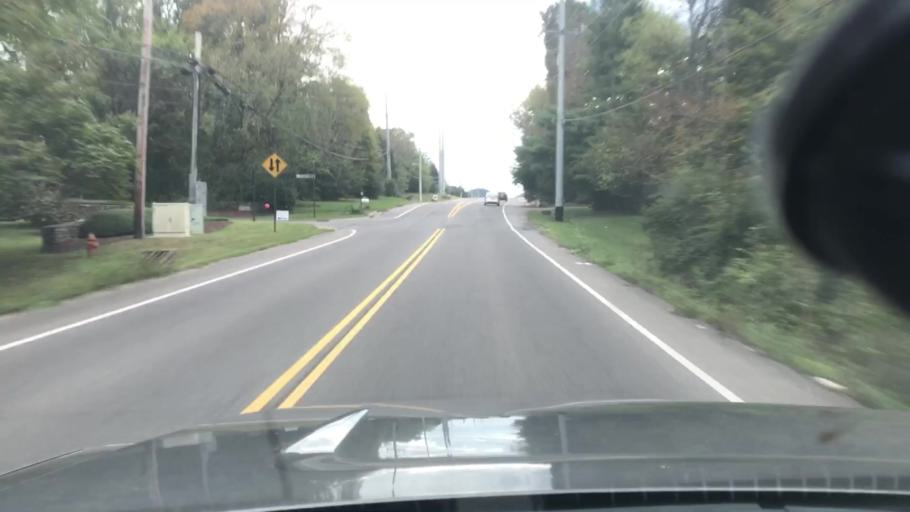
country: US
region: Tennessee
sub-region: Davidson County
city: Forest Hills
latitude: 36.0520
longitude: -86.8589
